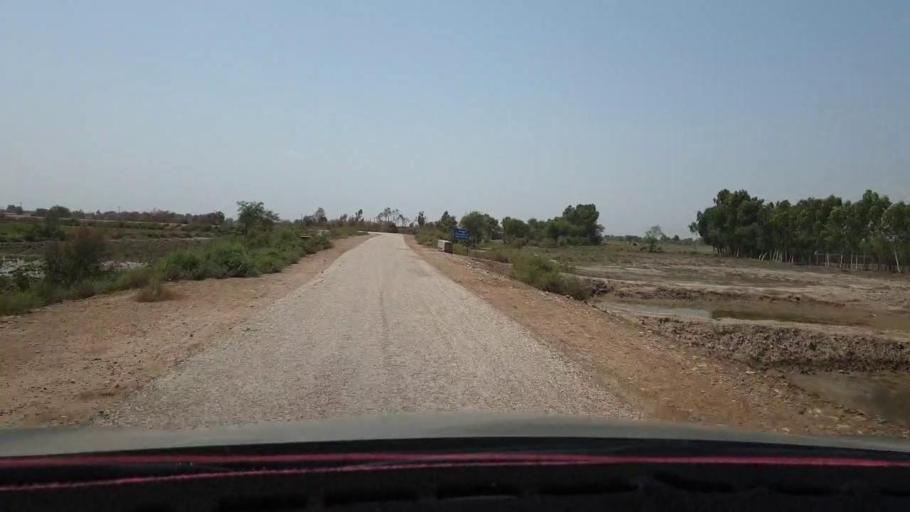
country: PK
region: Sindh
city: Warah
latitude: 27.5076
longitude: 67.7162
